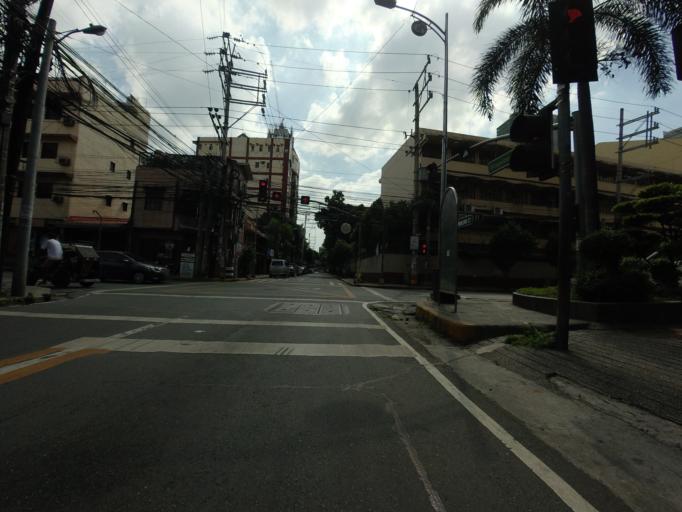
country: PH
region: Metro Manila
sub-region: City of Manila
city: Port Area
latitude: 14.5656
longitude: 120.9969
